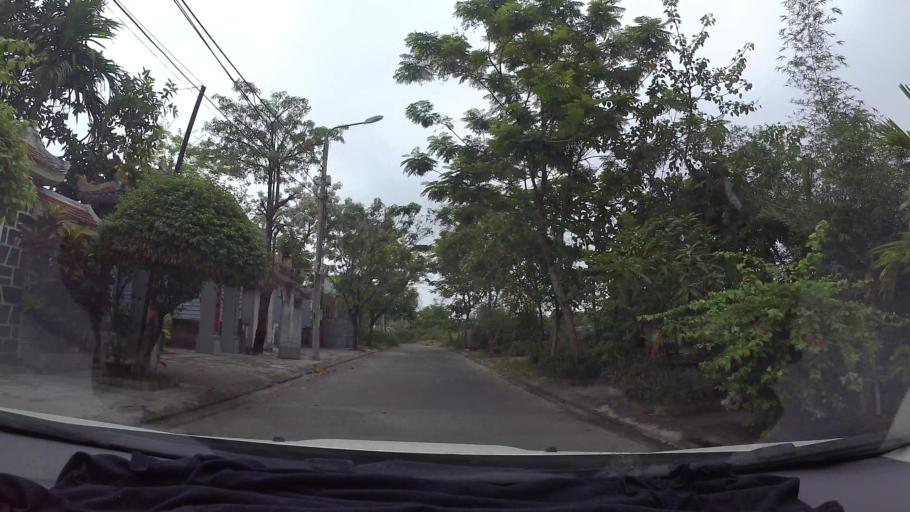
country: VN
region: Da Nang
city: Lien Chieu
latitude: 16.0746
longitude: 108.1669
